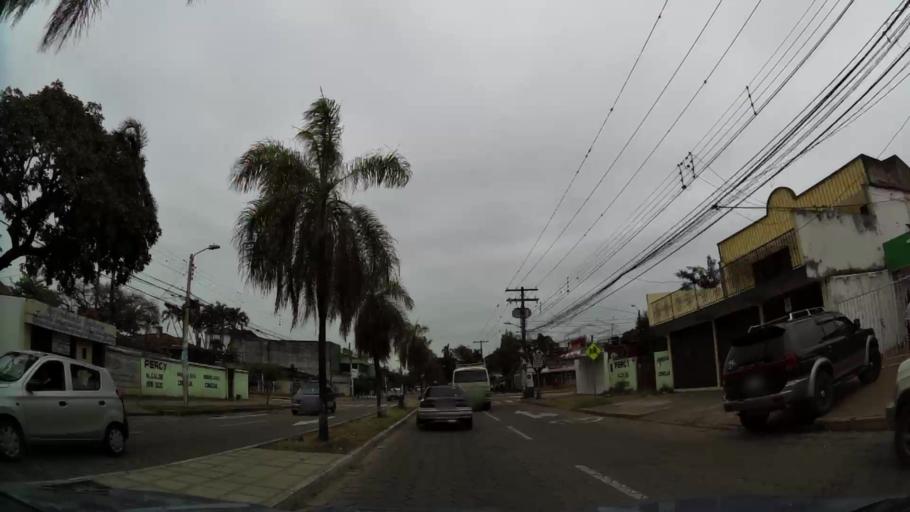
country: BO
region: Santa Cruz
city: Santa Cruz de la Sierra
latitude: -17.7893
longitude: -63.1746
